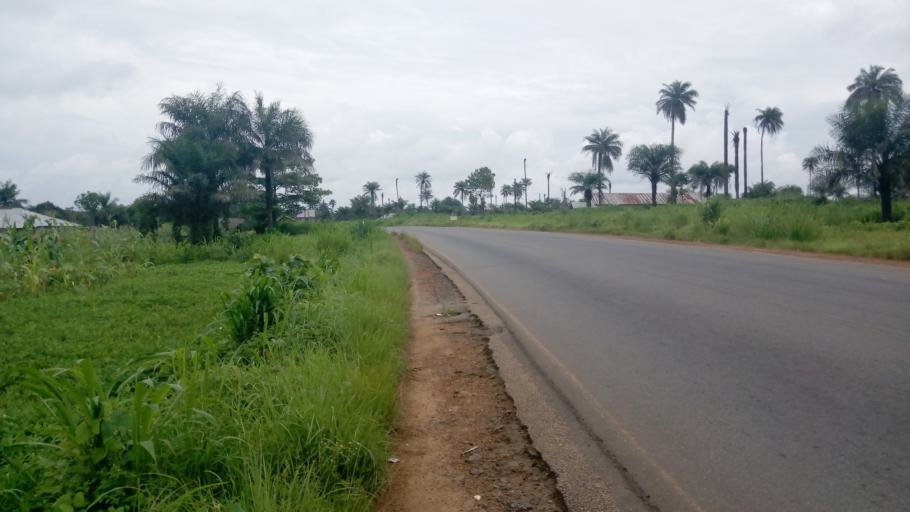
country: SL
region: Northern Province
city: Port Loko
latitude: 8.5022
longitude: -12.7584
